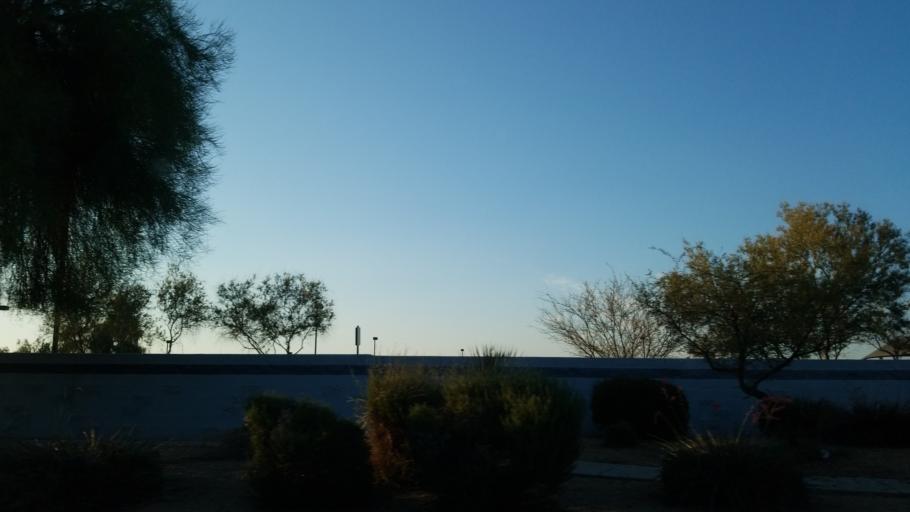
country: US
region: Arizona
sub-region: Maricopa County
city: Glendale
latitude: 33.6344
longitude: -112.1095
